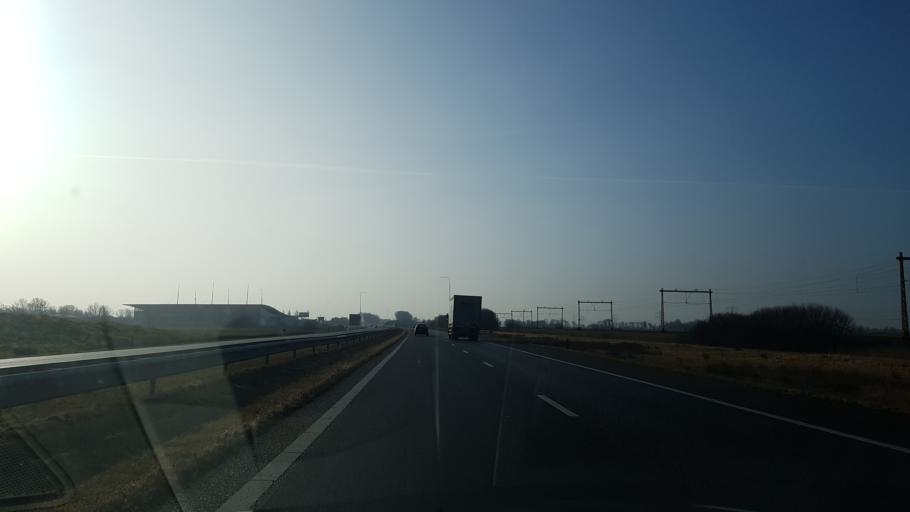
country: NL
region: Friesland
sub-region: Gemeente Boarnsterhim
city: Grou
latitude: 53.1034
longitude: 5.8165
